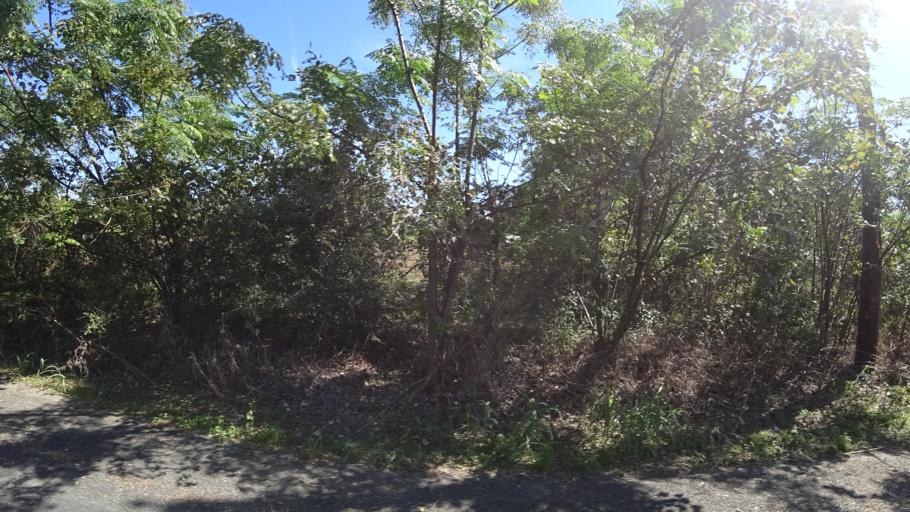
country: US
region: Texas
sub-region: Travis County
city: Austin
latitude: 30.2753
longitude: -97.6755
